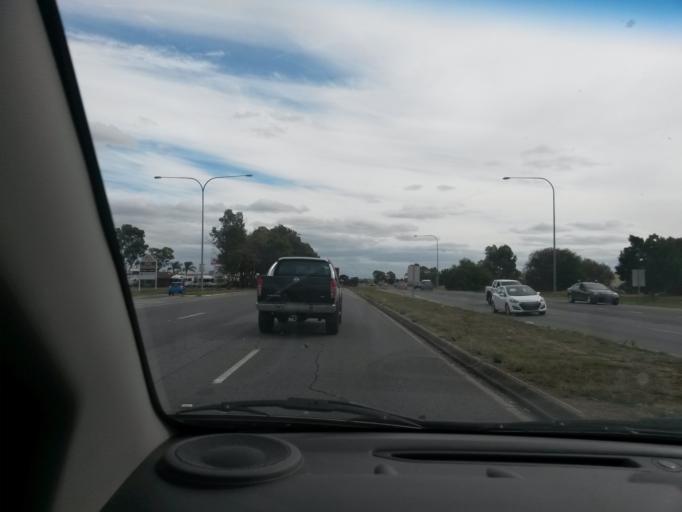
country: AU
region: South Australia
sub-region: Salisbury
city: Salisbury
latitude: -34.7931
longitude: 138.6458
